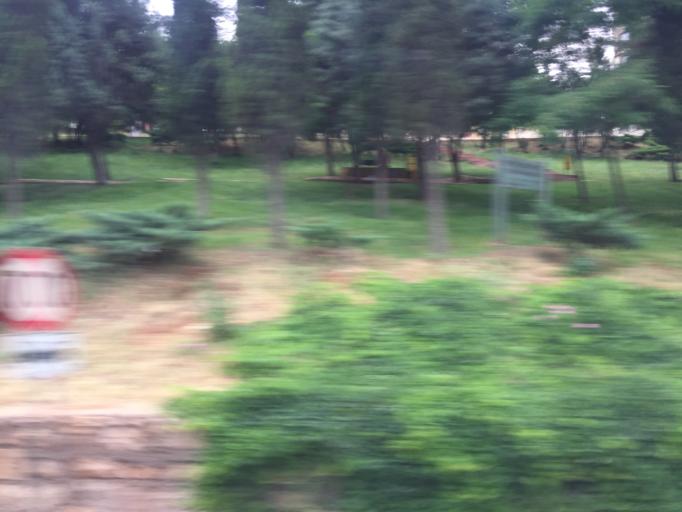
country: TR
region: Gaziantep
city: Gaziantep
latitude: 37.0544
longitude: 37.4176
